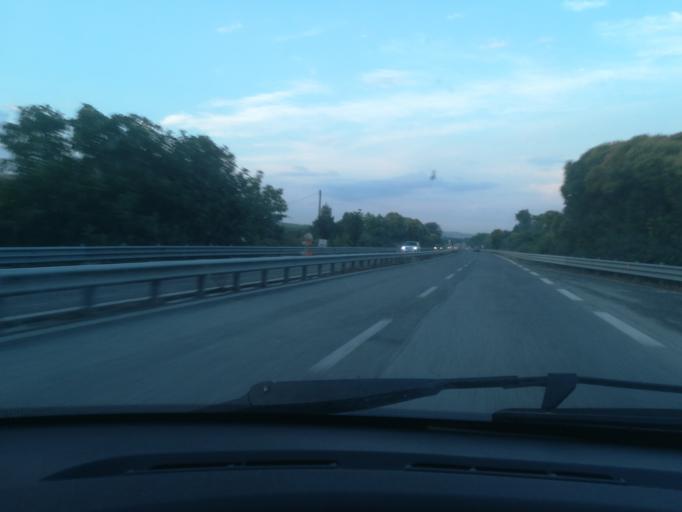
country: IT
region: The Marches
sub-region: Provincia di Macerata
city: Sforzacosta
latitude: 43.2481
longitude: 13.4327
